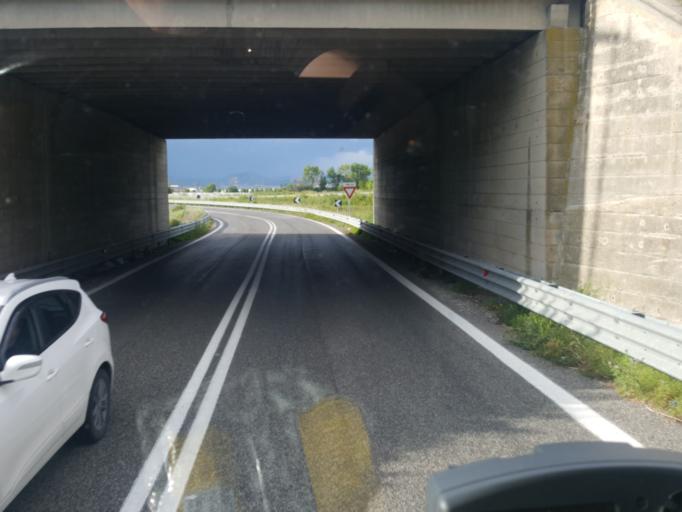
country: IT
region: Campania
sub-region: Provincia di Napoli
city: Pascarola
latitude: 40.9730
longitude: 14.3314
